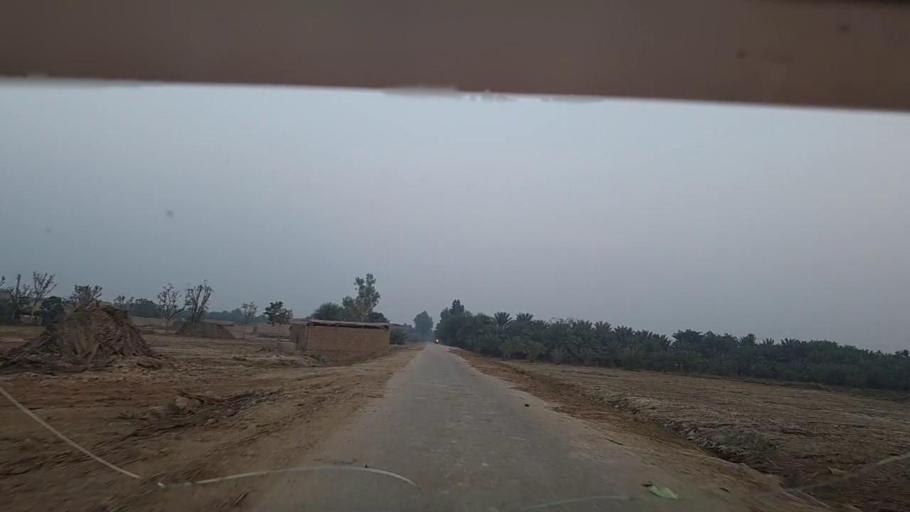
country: PK
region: Sindh
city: Khairpur
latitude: 27.5763
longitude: 68.7207
